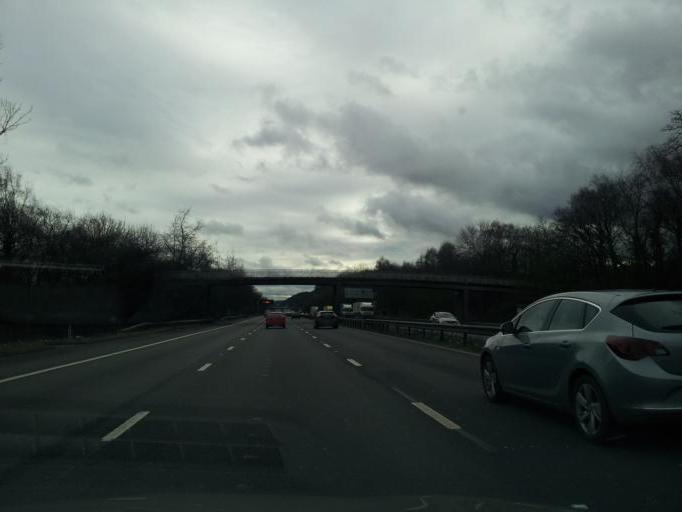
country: GB
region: England
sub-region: Staffordshire
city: Newcastle under Lyme
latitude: 52.9578
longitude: -2.2196
